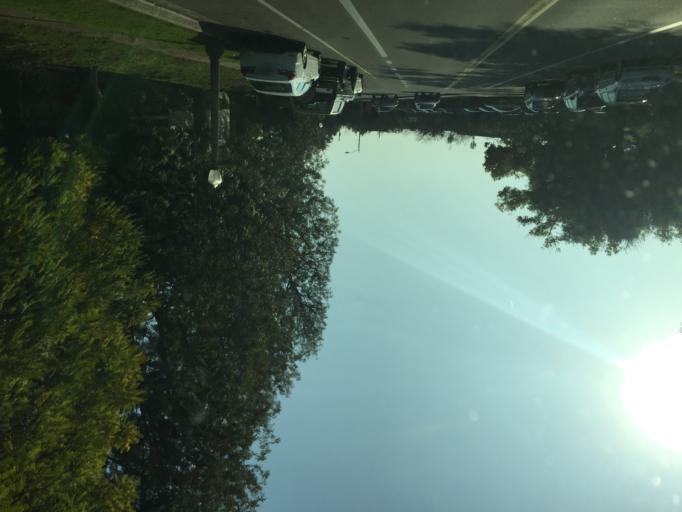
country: US
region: California
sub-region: Los Angeles County
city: South Pasadena
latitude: 34.1155
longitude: -118.1484
